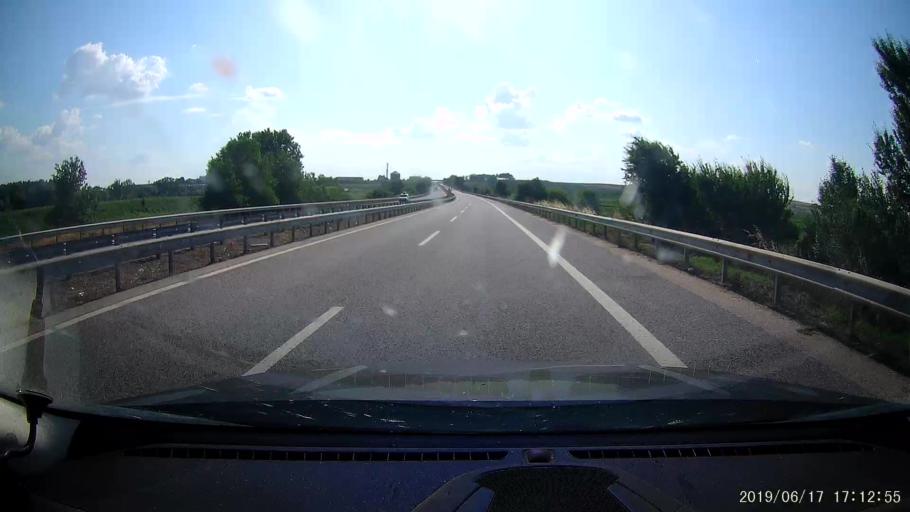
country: TR
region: Edirne
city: Edirne
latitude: 41.7013
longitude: 26.5514
